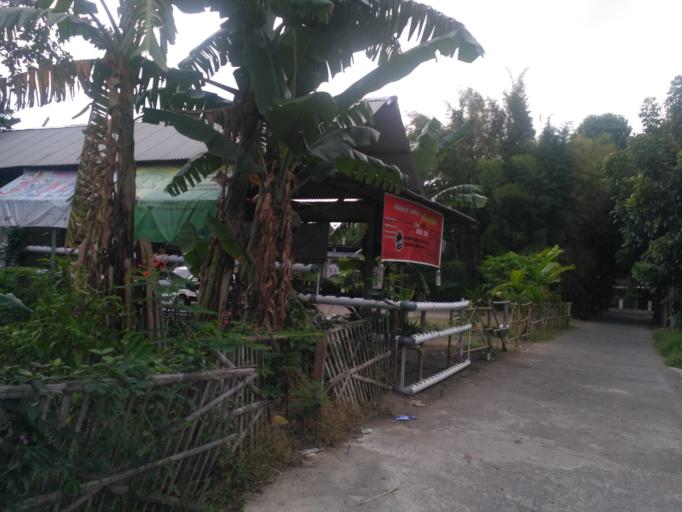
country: ID
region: Daerah Istimewa Yogyakarta
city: Melati
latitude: -7.7511
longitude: 110.3645
